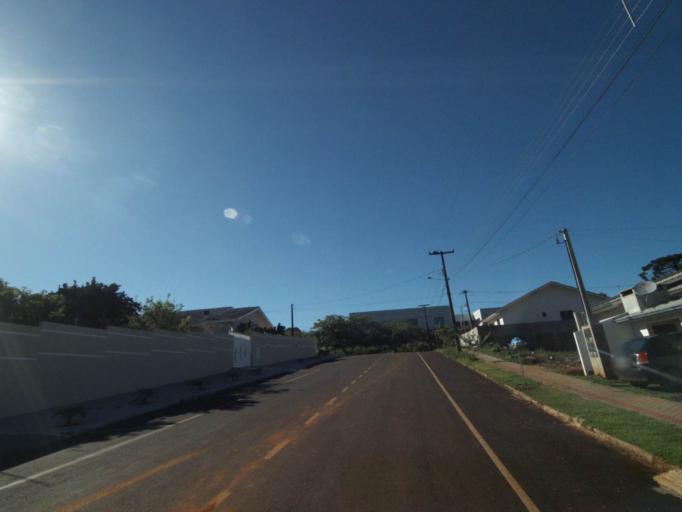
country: BR
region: Santa Catarina
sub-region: Sao Lourenco Do Oeste
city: Sao Lourenco dOeste
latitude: -26.2653
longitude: -52.7851
